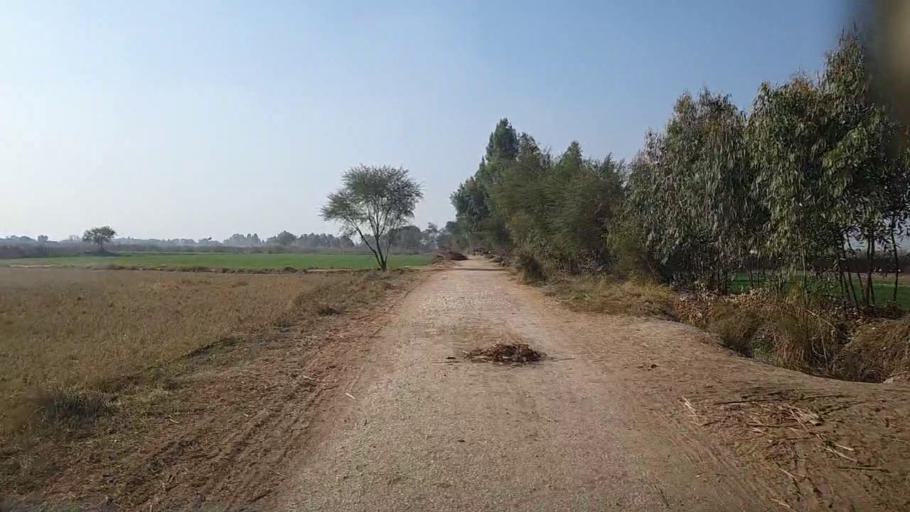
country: PK
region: Sindh
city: Mirpur Mathelo
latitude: 27.9023
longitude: 69.6330
